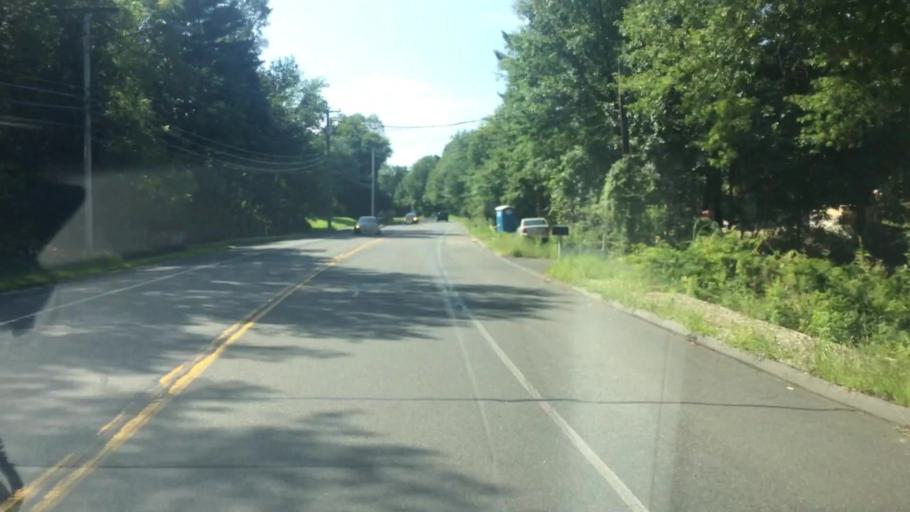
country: US
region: Massachusetts
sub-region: Hampshire County
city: South Amherst
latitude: 42.3541
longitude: -72.5206
